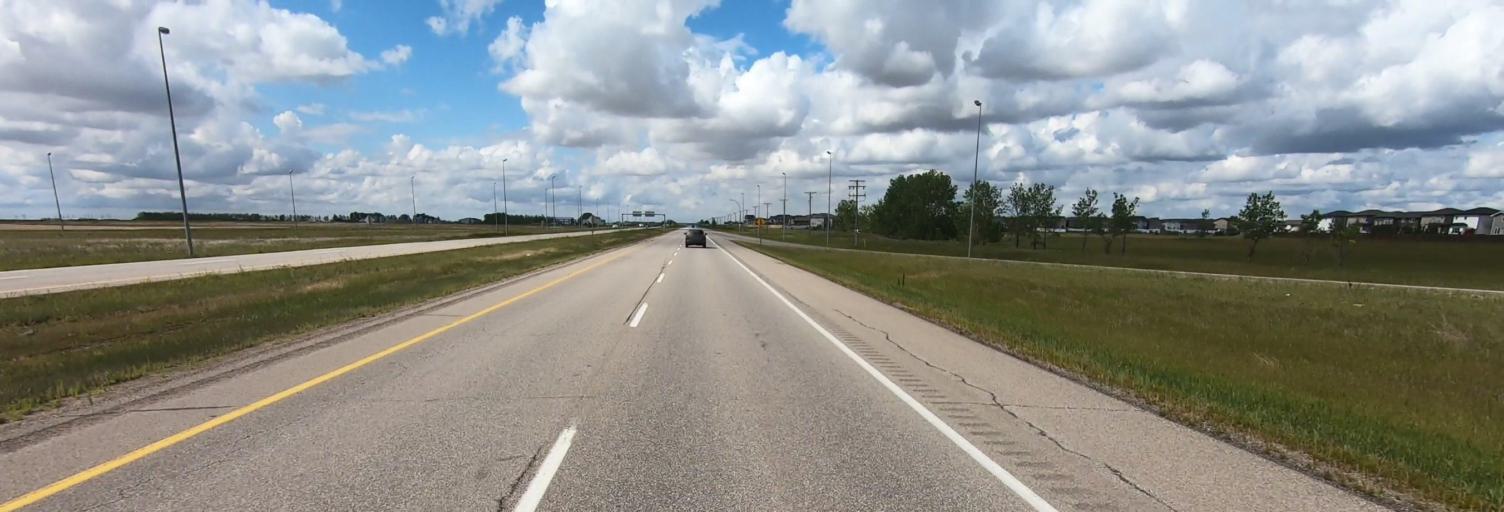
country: CA
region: Saskatchewan
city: Regina
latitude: 50.3969
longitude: -104.6471
